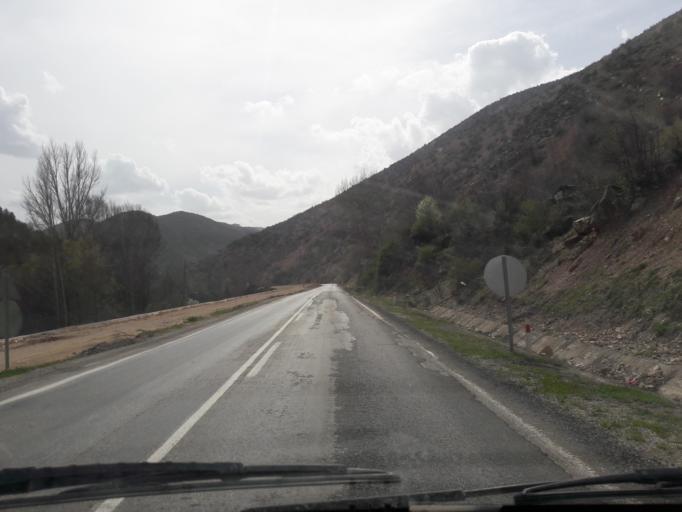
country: TR
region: Gumushane
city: Kale
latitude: 40.3928
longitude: 39.5863
